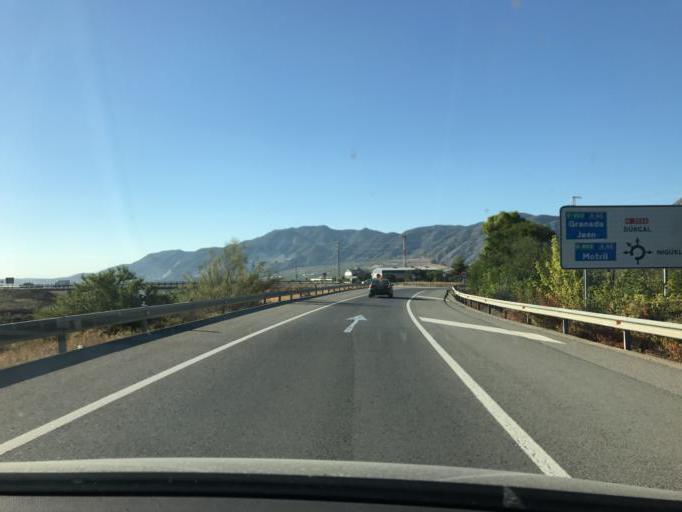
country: ES
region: Andalusia
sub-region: Provincia de Granada
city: Durcal
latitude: 36.9723
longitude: -3.5586
